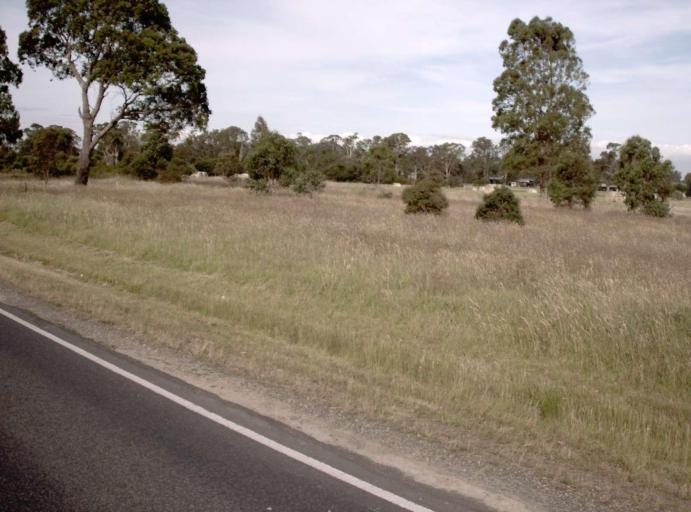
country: AU
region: Victoria
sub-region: Latrobe
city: Traralgon
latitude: -38.0664
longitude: 146.6178
